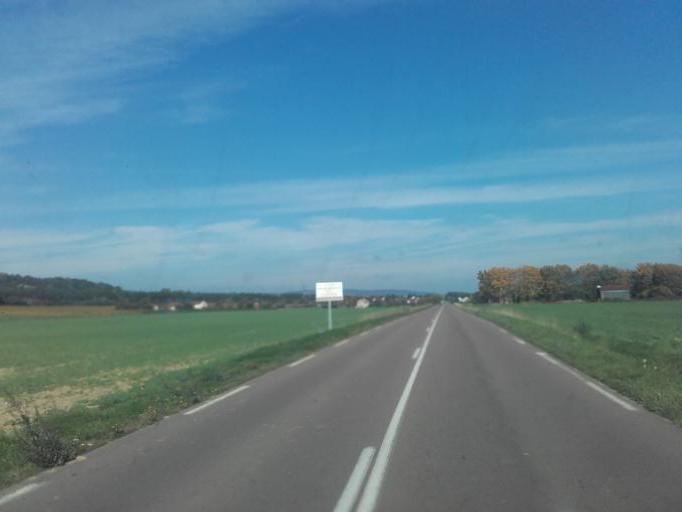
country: FR
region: Bourgogne
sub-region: Departement de Saone-et-Loire
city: Rully
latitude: 46.8855
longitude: 4.7523
